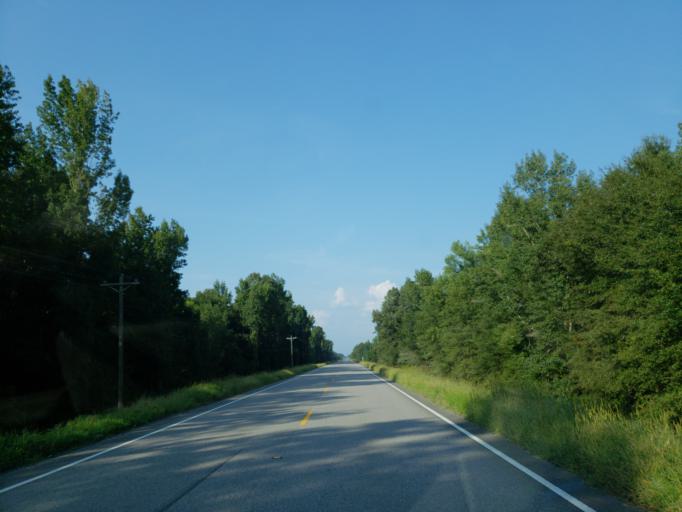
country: US
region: Alabama
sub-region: Sumter County
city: Livingston
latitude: 32.7058
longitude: -88.0855
